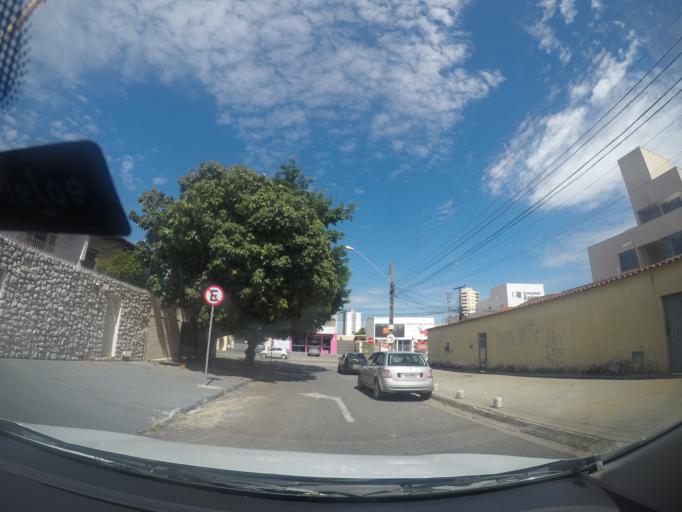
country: BR
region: Goias
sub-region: Goiania
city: Goiania
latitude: -16.7225
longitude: -49.2684
